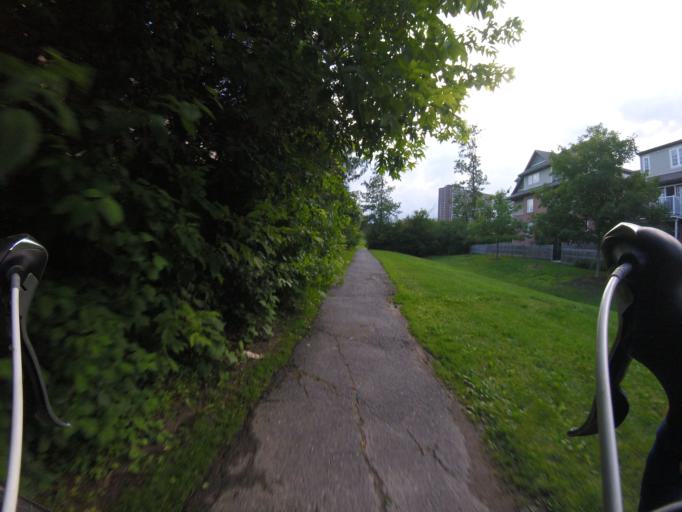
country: CA
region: Ontario
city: Bells Corners
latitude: 45.3690
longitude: -75.7809
